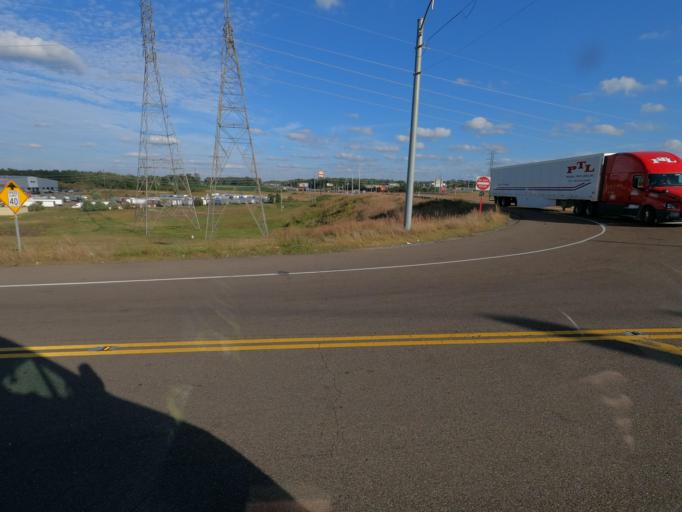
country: US
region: Tennessee
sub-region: Madison County
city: Jackson
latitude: 35.6816
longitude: -88.7796
